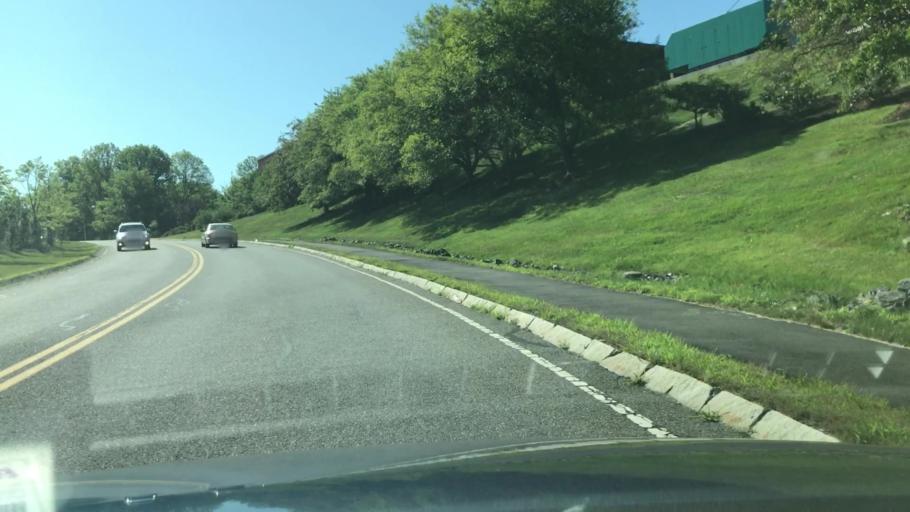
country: US
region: Massachusetts
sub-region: Middlesex County
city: Marlborough
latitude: 42.3355
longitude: -71.5931
